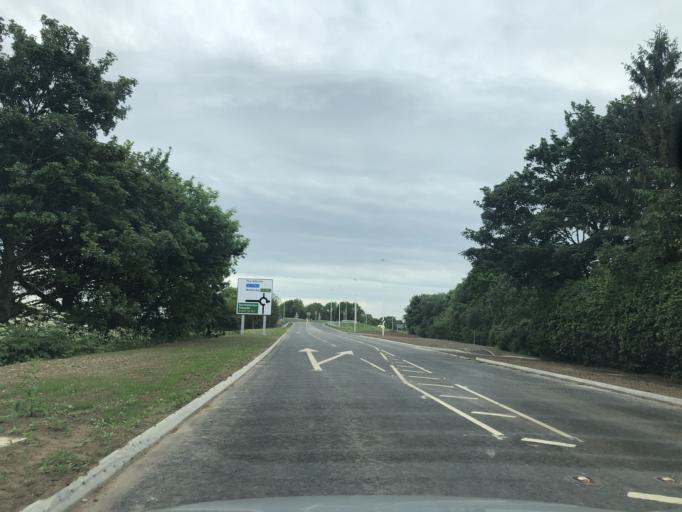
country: GB
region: England
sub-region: North Yorkshire
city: Thirsk
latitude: 54.2078
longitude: -1.3585
